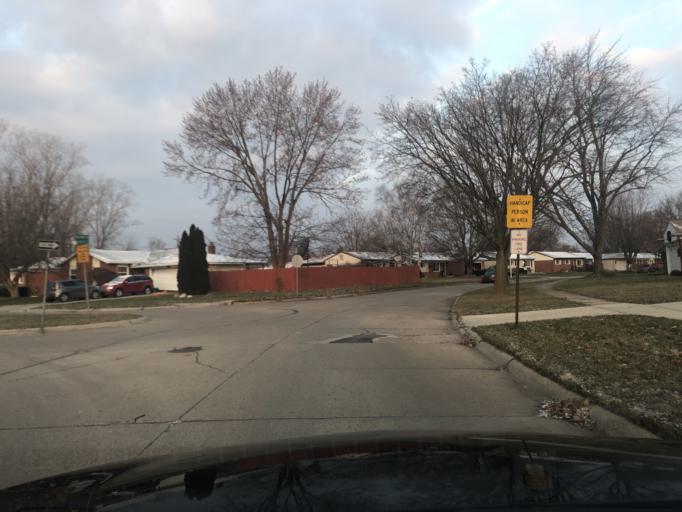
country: US
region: Michigan
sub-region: Wayne County
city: Romulus
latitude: 42.2319
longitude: -83.3826
